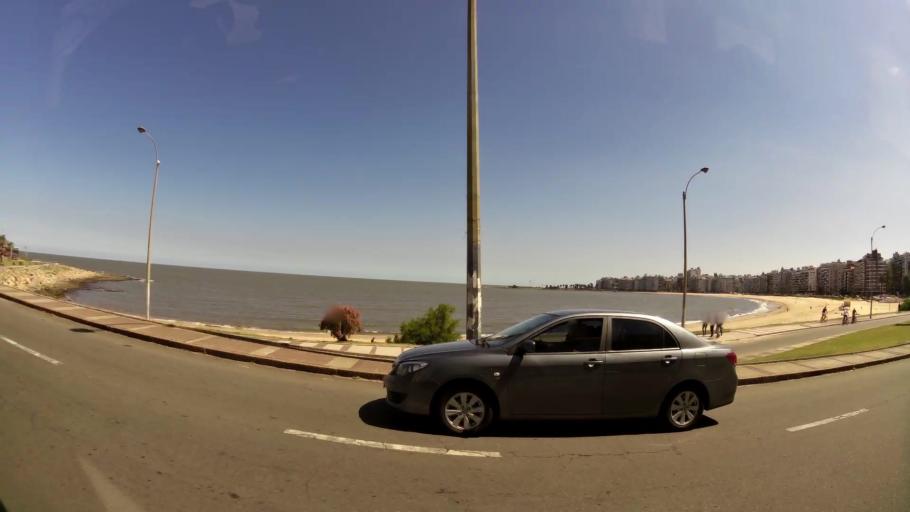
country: UY
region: Montevideo
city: Montevideo
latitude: -34.9097
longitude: -56.1407
